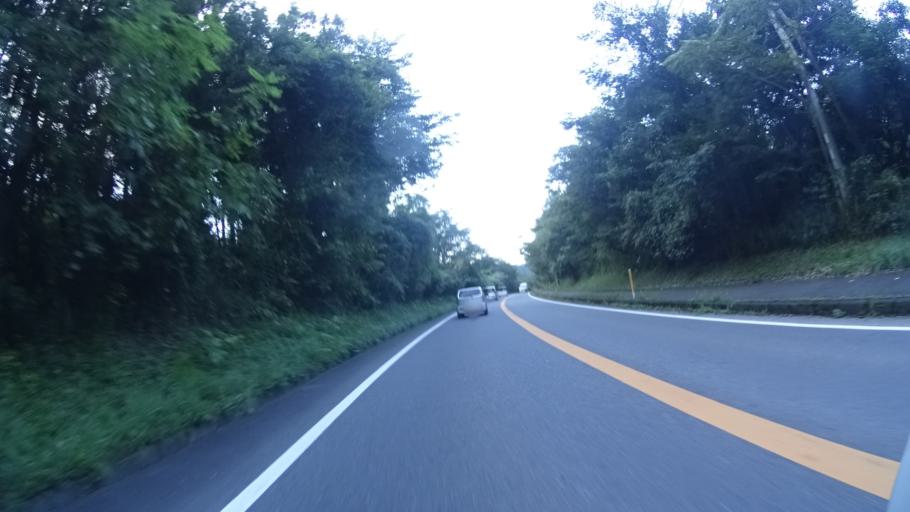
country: JP
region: Oita
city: Beppu
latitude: 33.3461
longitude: 131.4291
